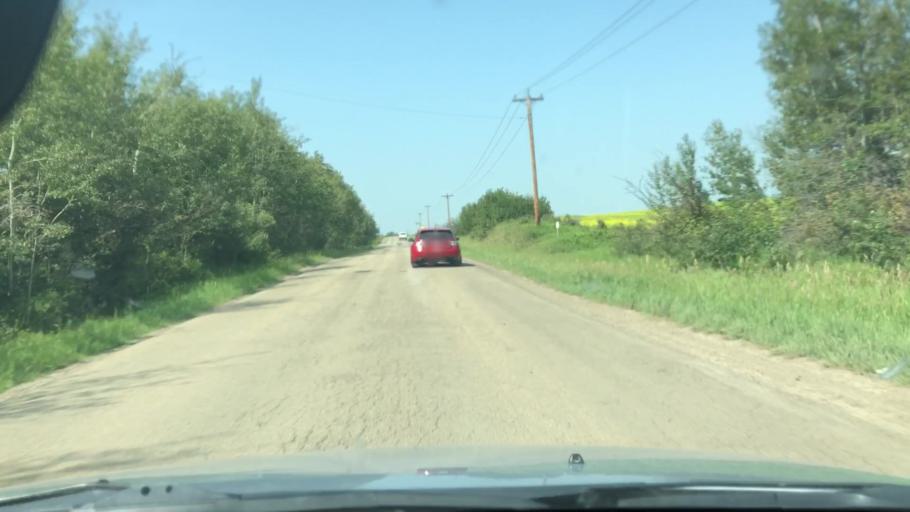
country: CA
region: Alberta
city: Devon
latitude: 53.5122
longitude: -113.7498
